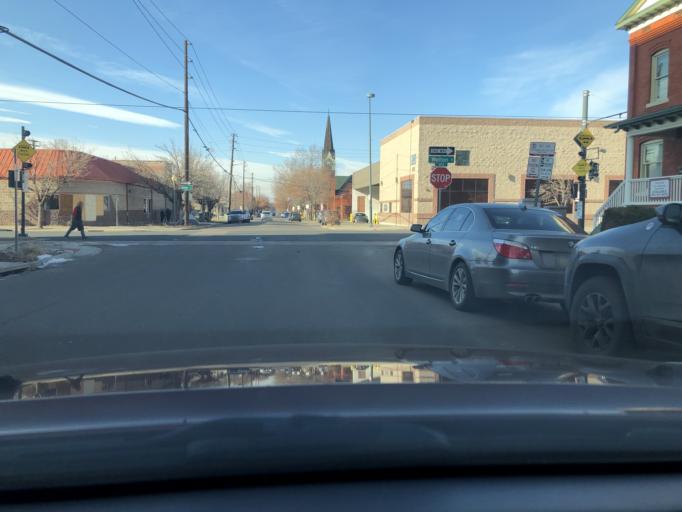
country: US
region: Colorado
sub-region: Denver County
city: Denver
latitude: 39.7527
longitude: -104.9802
